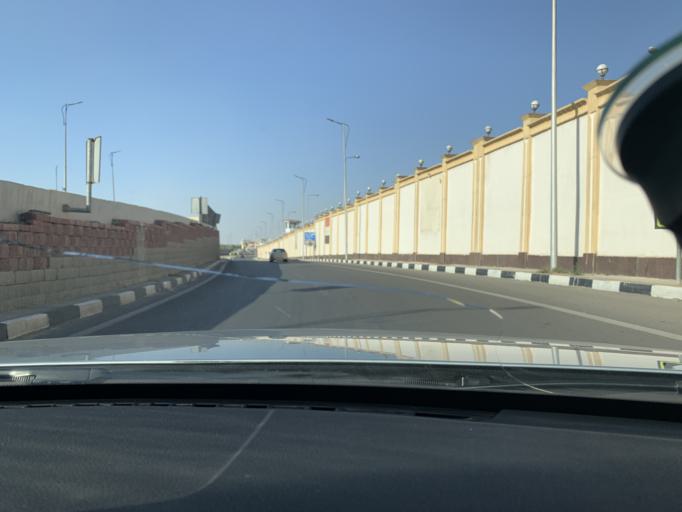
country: EG
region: Muhafazat al Qahirah
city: Cairo
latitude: 30.0506
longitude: 31.4104
